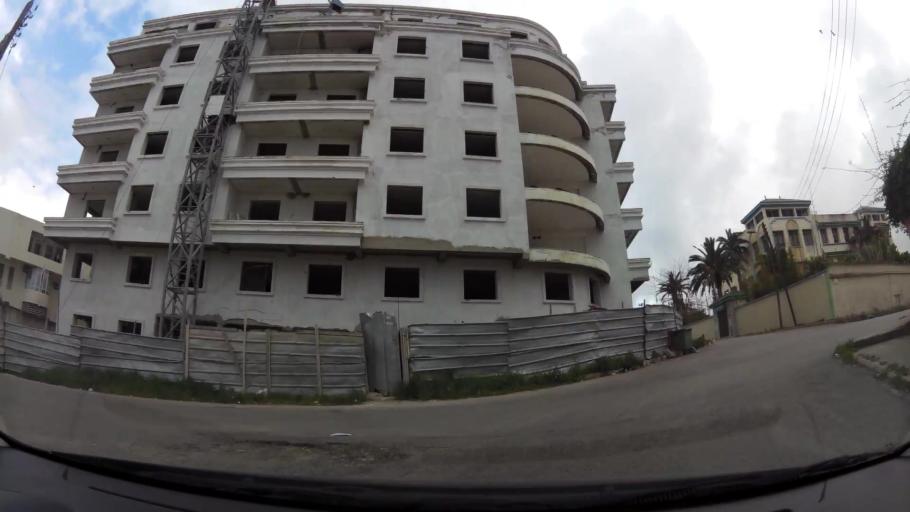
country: MA
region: Tanger-Tetouan
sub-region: Tanger-Assilah
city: Tangier
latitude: 35.7661
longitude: -5.8004
